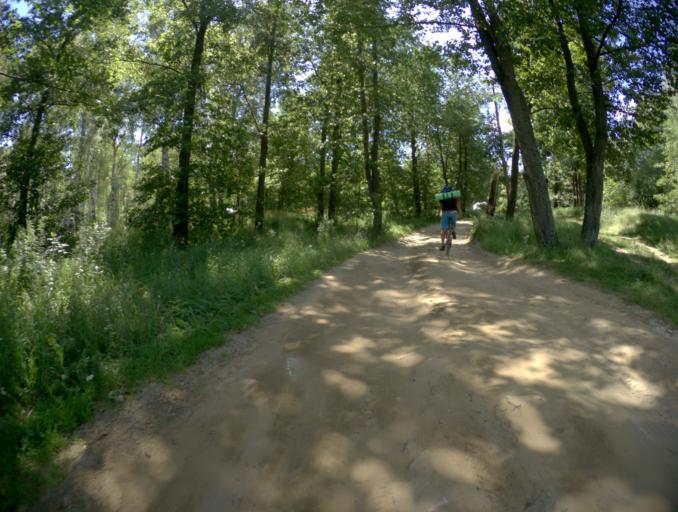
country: RU
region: Nizjnij Novgorod
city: Sitniki
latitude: 56.4591
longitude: 44.0171
